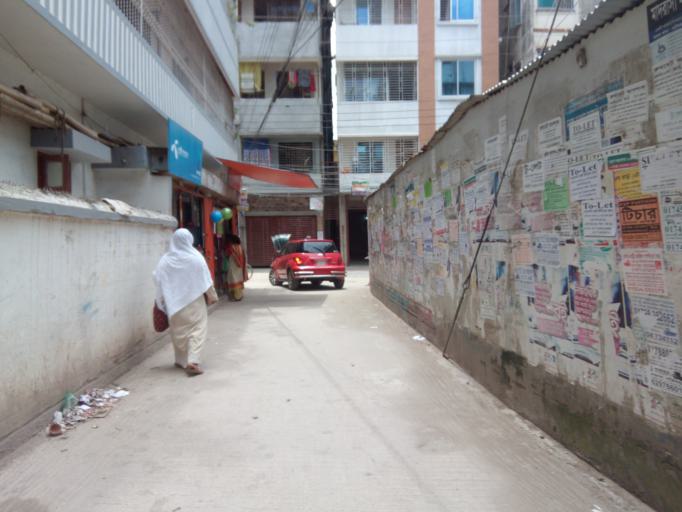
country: BD
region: Dhaka
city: Azimpur
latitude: 23.7433
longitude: 90.3894
